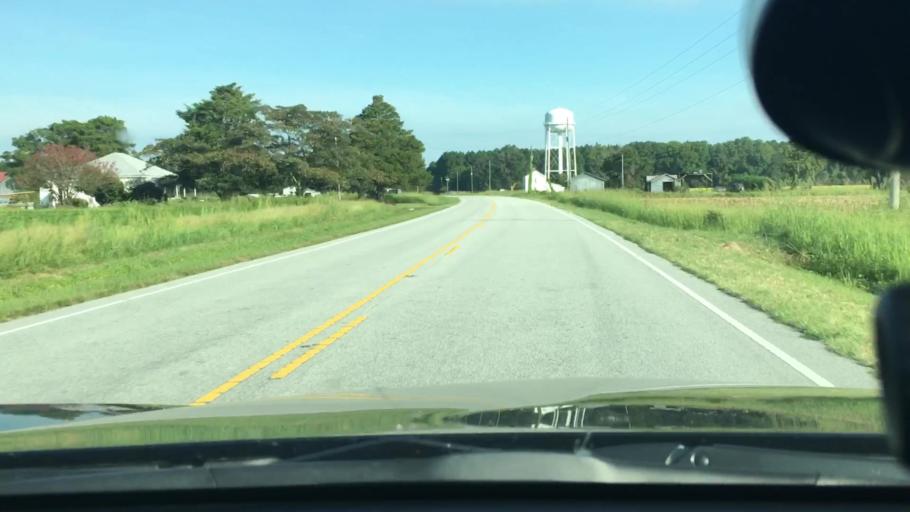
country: US
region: North Carolina
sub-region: Pitt County
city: Farmville
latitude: 35.7090
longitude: -77.5193
